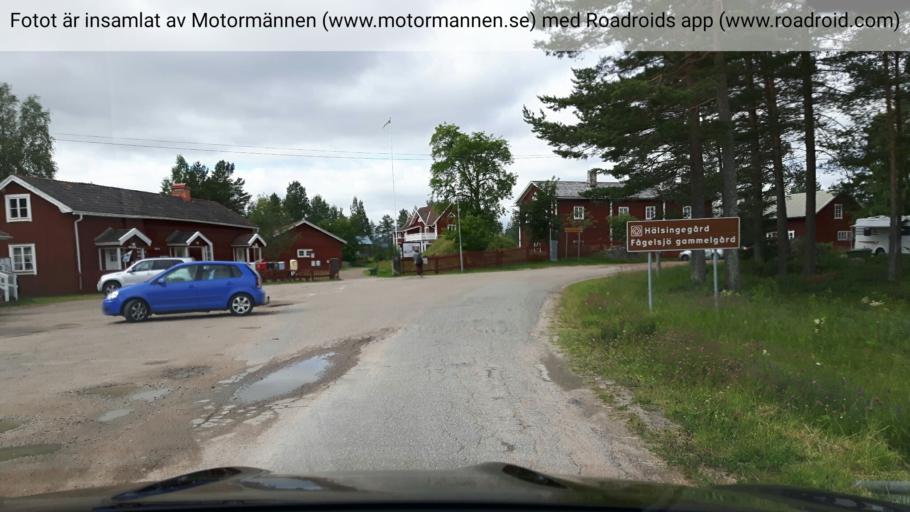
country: SE
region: Jaemtland
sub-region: Harjedalens Kommun
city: Sveg
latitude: 61.7968
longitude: 14.6364
